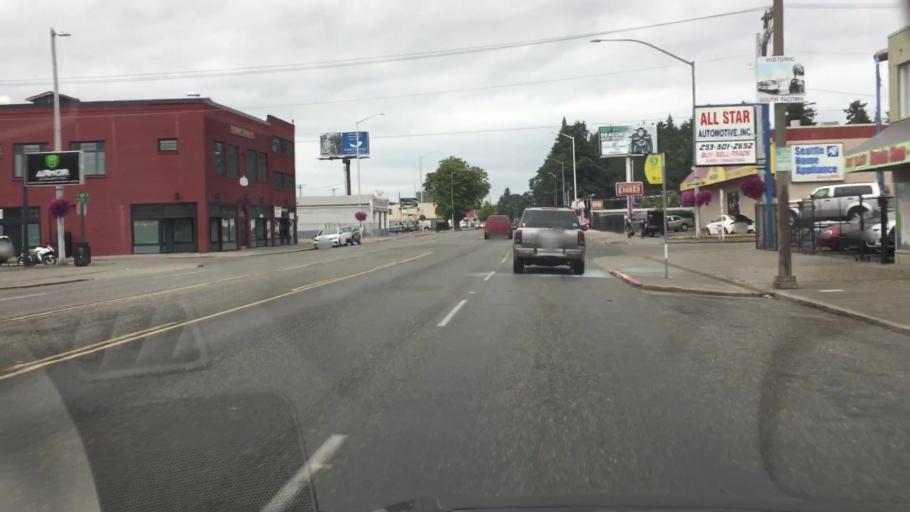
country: US
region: Washington
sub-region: Pierce County
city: Fircrest
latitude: 47.2094
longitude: -122.4837
